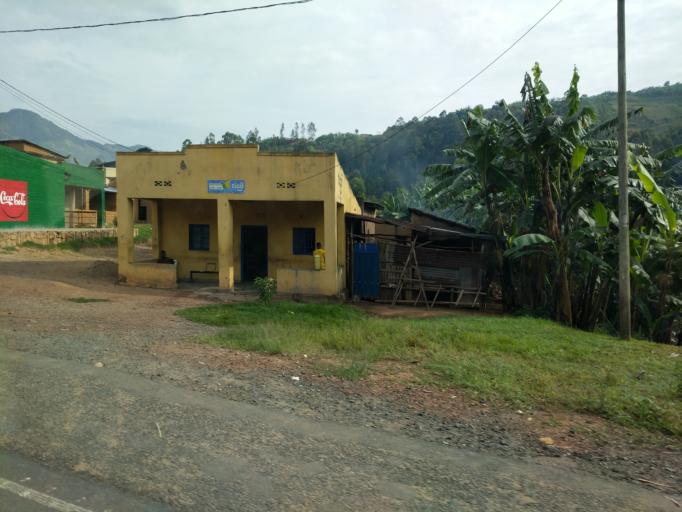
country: RW
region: Northern Province
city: Musanze
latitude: -1.6576
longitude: 29.8258
